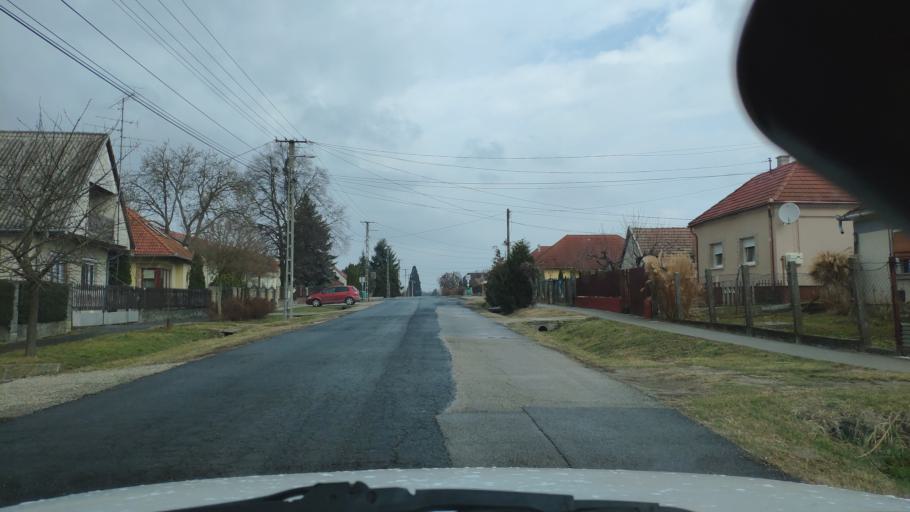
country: HU
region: Zala
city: Nagykanizsa
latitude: 46.4118
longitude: 16.9986
